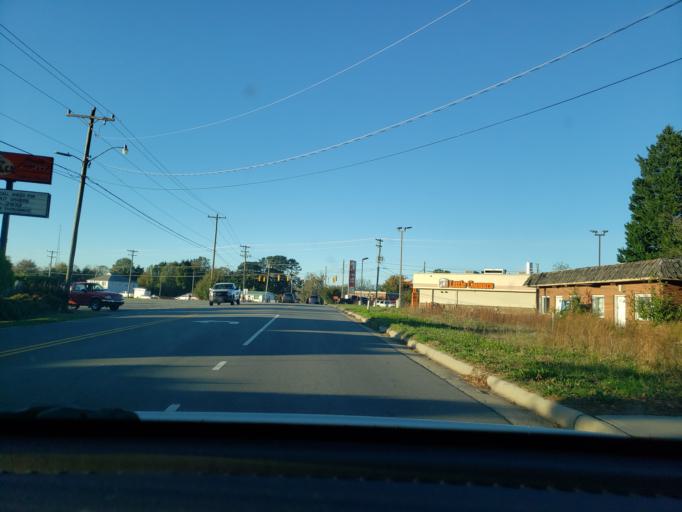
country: US
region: North Carolina
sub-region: Forsyth County
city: Walkertown
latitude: 36.1670
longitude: -80.1479
